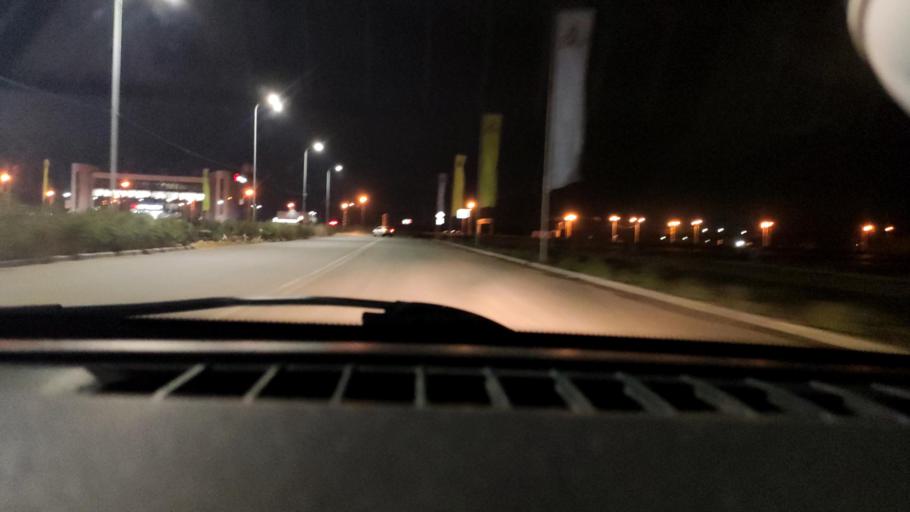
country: RU
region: Samara
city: Samara
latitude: 53.1356
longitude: 50.1707
